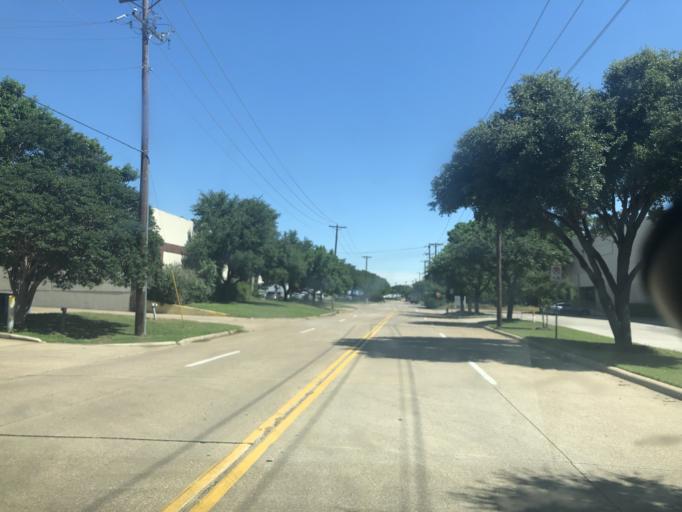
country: US
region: Texas
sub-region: Tarrant County
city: Euless
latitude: 32.7923
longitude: -97.0396
